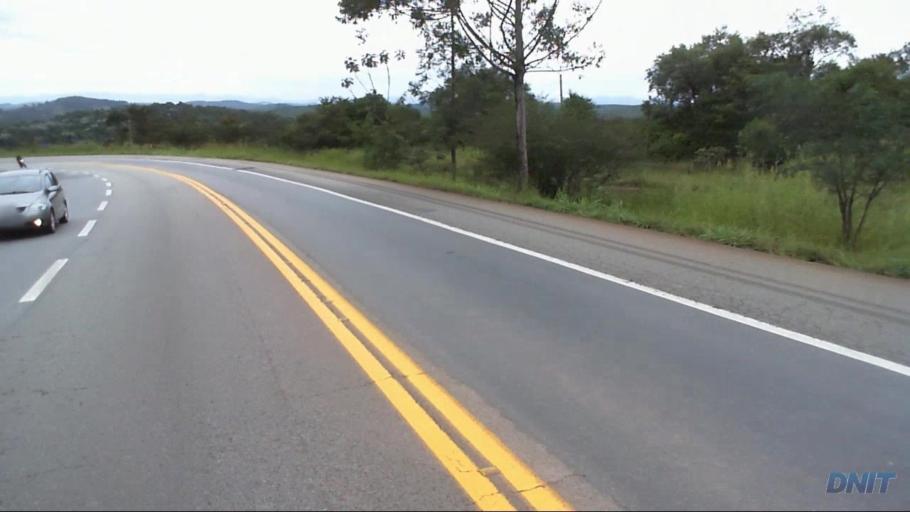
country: BR
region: Minas Gerais
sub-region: Caete
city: Caete
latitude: -19.7399
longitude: -43.5164
